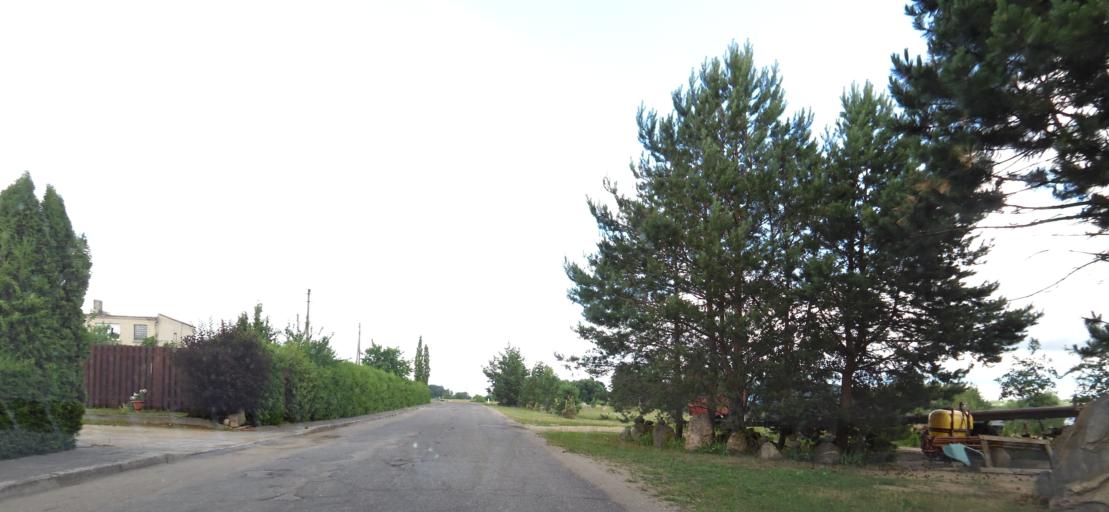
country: LT
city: Kupiskis
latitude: 55.8468
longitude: 24.9615
